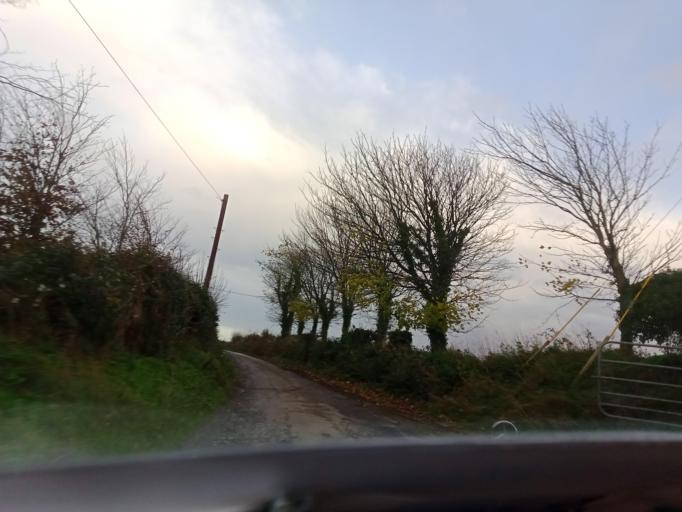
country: IE
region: Leinster
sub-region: Loch Garman
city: New Ross
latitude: 52.3459
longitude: -7.0182
